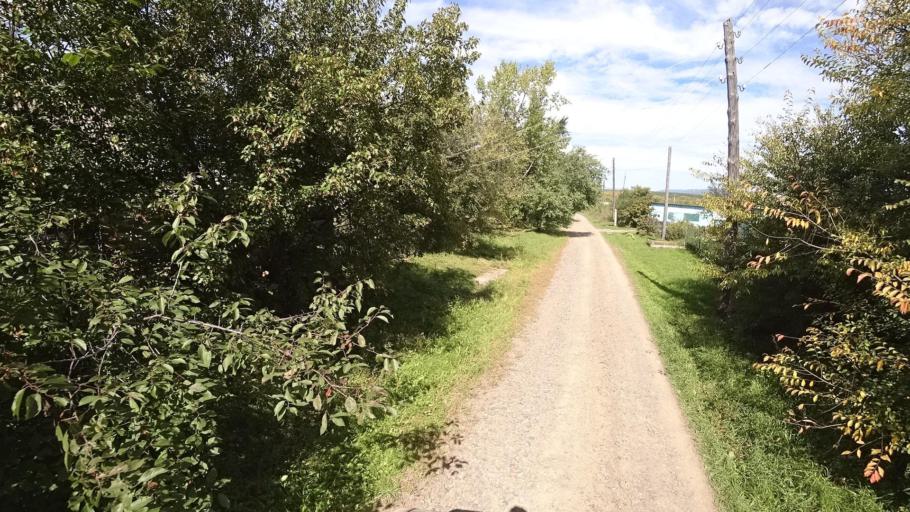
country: RU
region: Primorskiy
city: Yakovlevka
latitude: 44.4336
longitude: 133.5587
